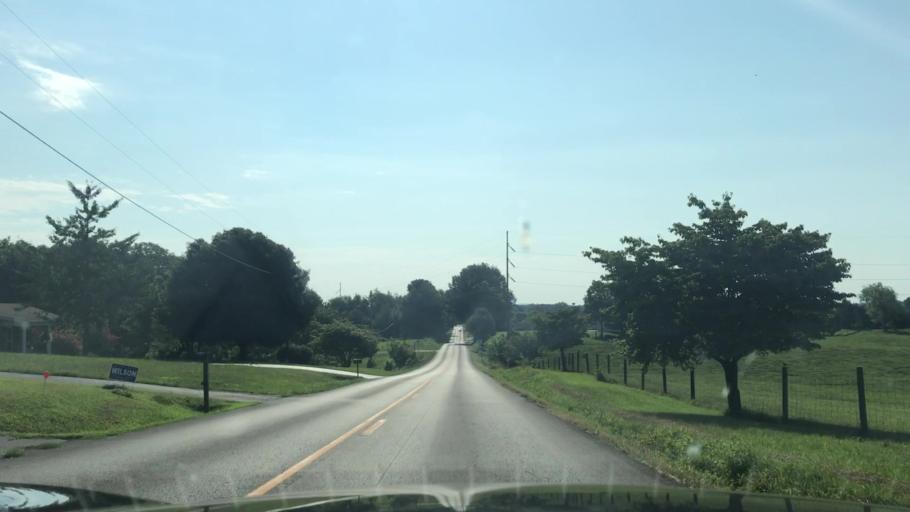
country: US
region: Kentucky
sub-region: Hart County
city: Horse Cave
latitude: 37.1676
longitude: -85.8178
